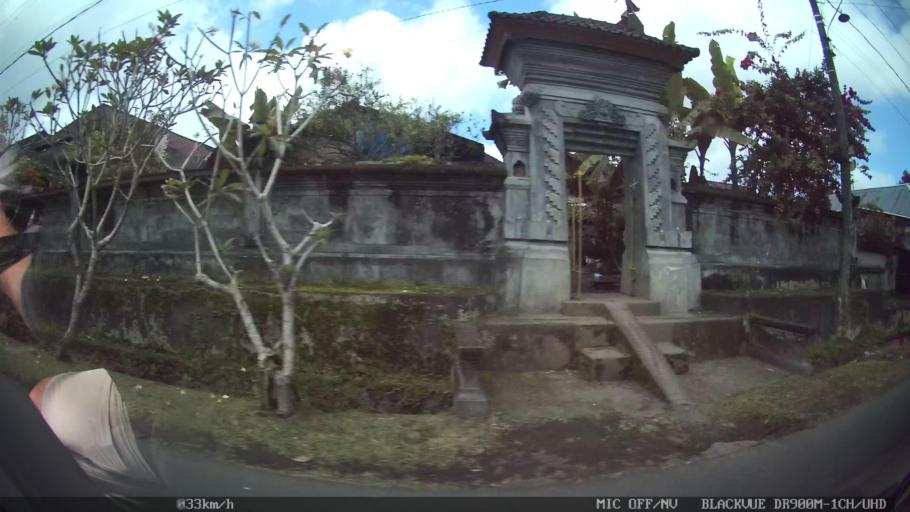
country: ID
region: Bali
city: Banjar Abuan
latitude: -8.4556
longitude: 115.3408
